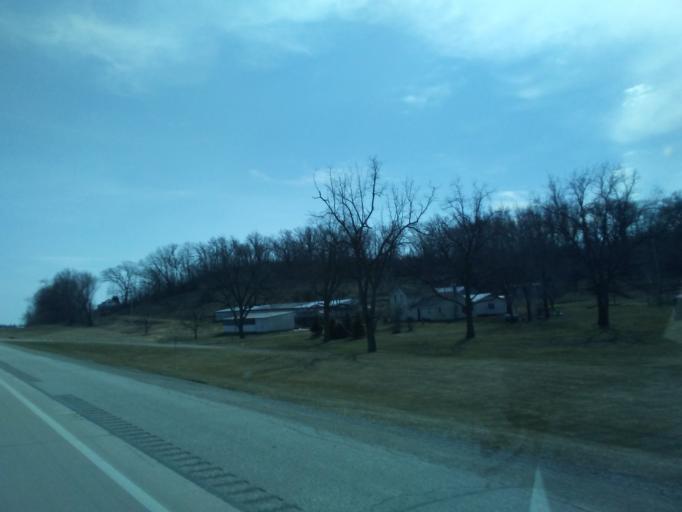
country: US
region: Minnesota
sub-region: Fillmore County
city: Preston
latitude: 43.7049
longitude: -92.1074
